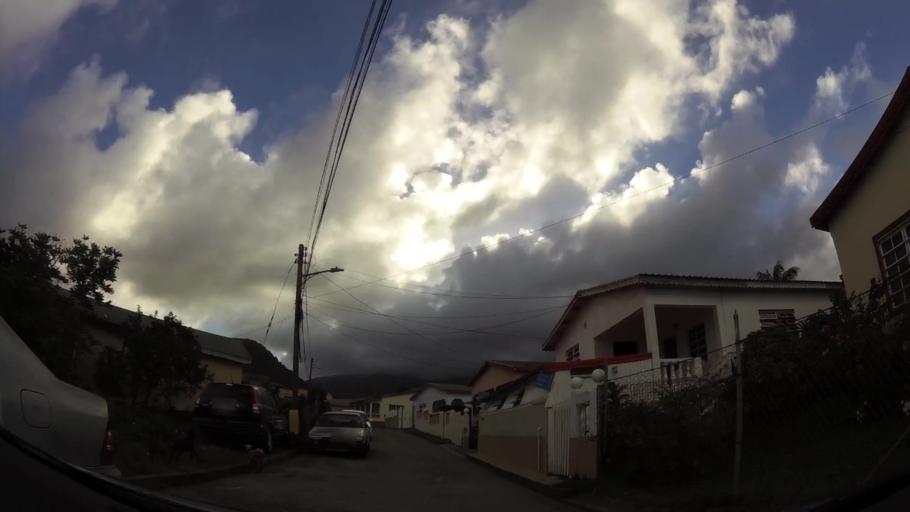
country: KN
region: Saint Mary Cayon
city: Cayon
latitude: 17.3508
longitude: -62.7276
